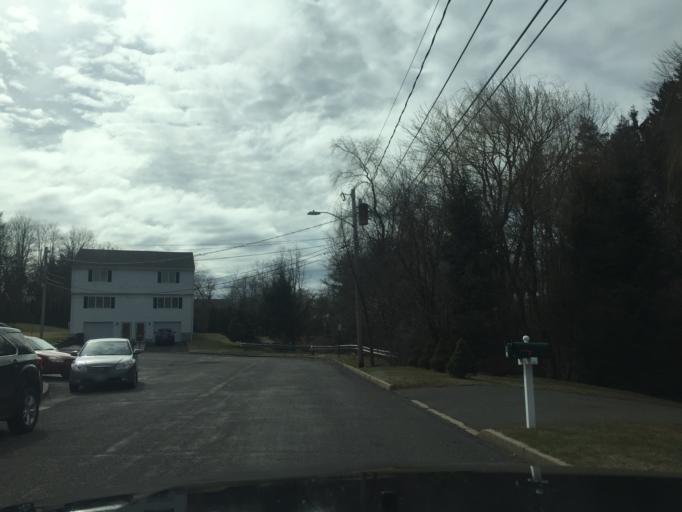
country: US
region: Connecticut
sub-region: Hartford County
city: New Britain
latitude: 41.6905
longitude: -72.7871
